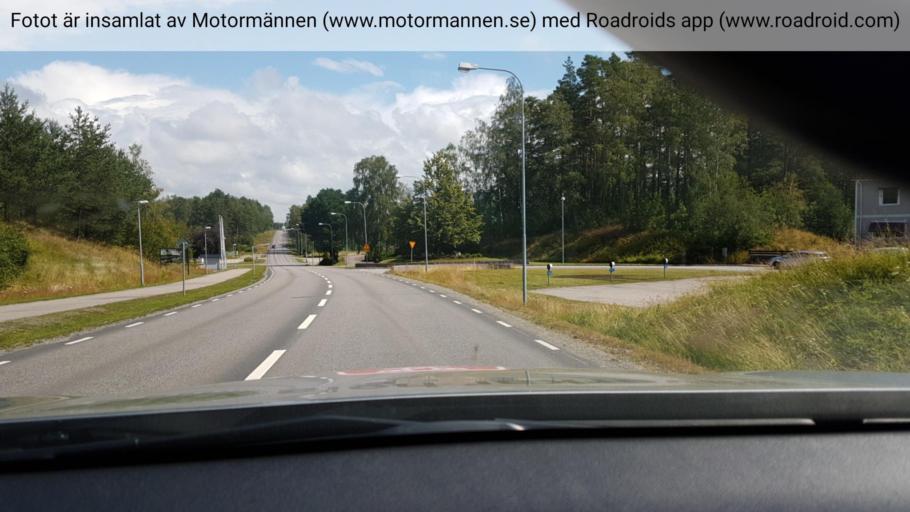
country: SE
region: Vaestra Goetaland
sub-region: Tranemo Kommun
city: Tranemo
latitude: 57.4867
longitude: 13.3551
